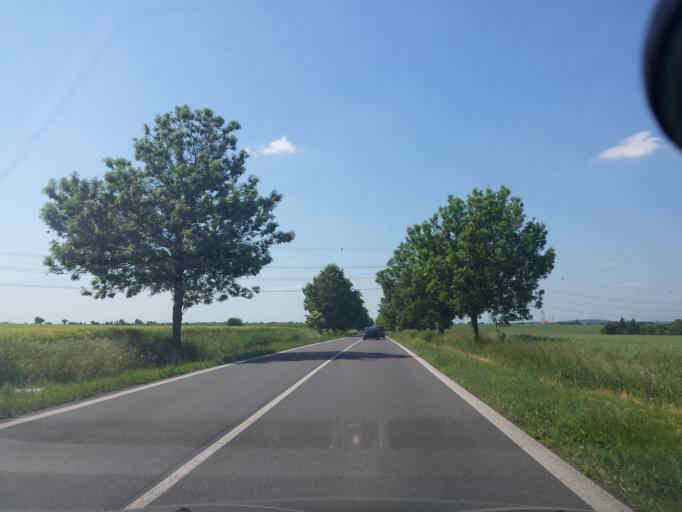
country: CZ
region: Central Bohemia
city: Horomerice
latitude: 50.1202
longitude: 14.3568
